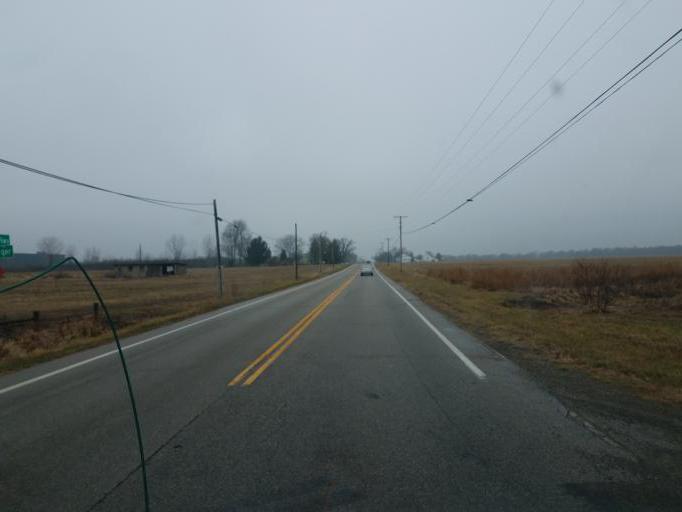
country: US
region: Ohio
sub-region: Union County
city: New California
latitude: 40.1959
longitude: -83.2971
